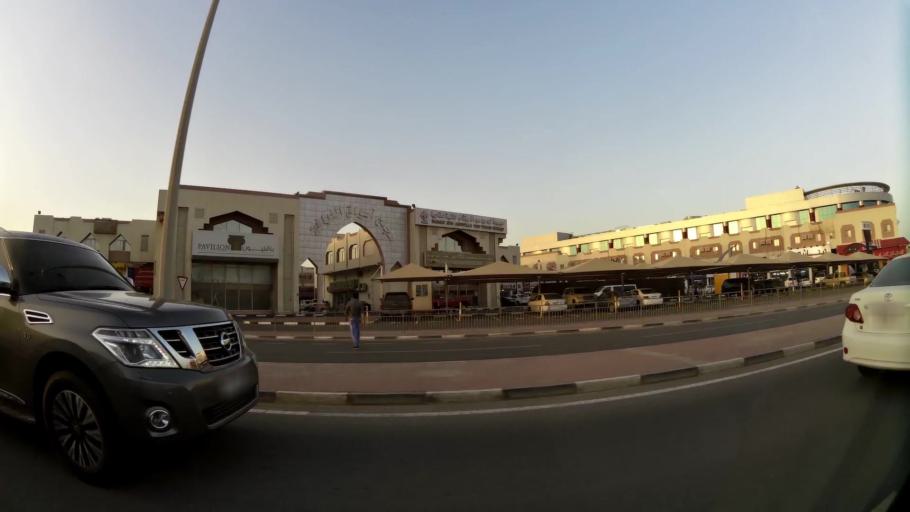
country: QA
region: Baladiyat ar Rayyan
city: Ar Rayyan
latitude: 25.3261
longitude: 51.4651
